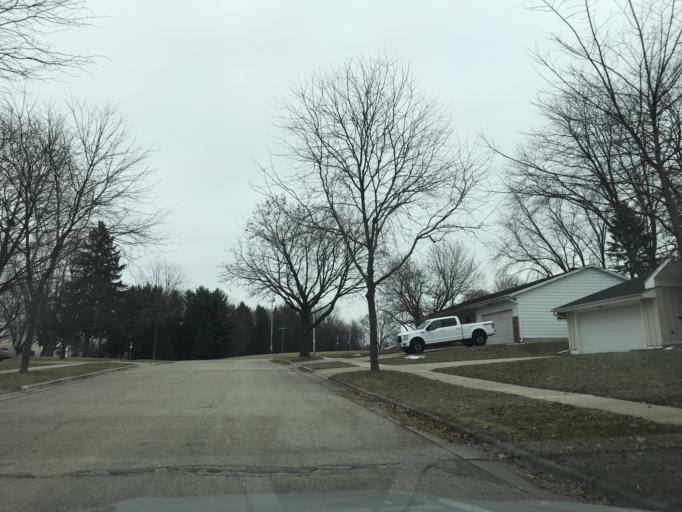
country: US
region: Wisconsin
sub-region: Dane County
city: Monona
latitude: 43.0955
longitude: -89.2991
